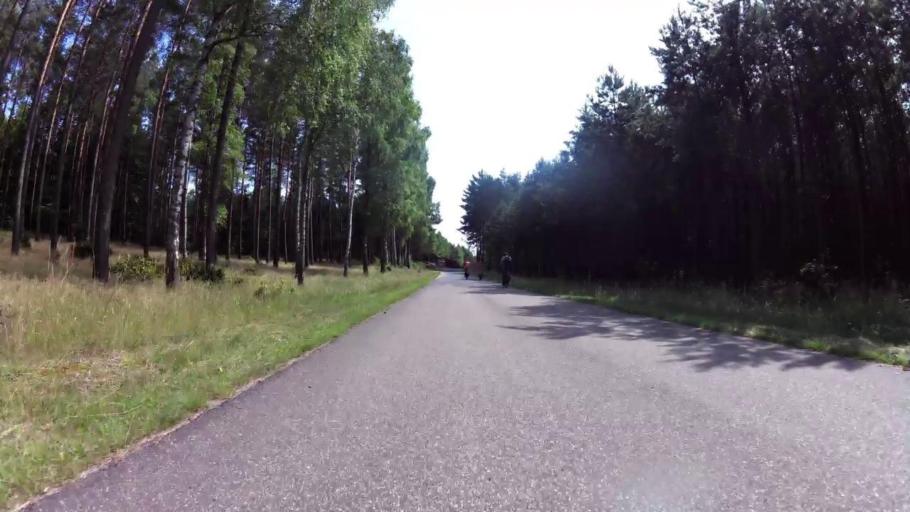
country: PL
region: West Pomeranian Voivodeship
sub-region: Powiat choszczenski
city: Drawno
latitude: 53.3478
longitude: 15.7036
